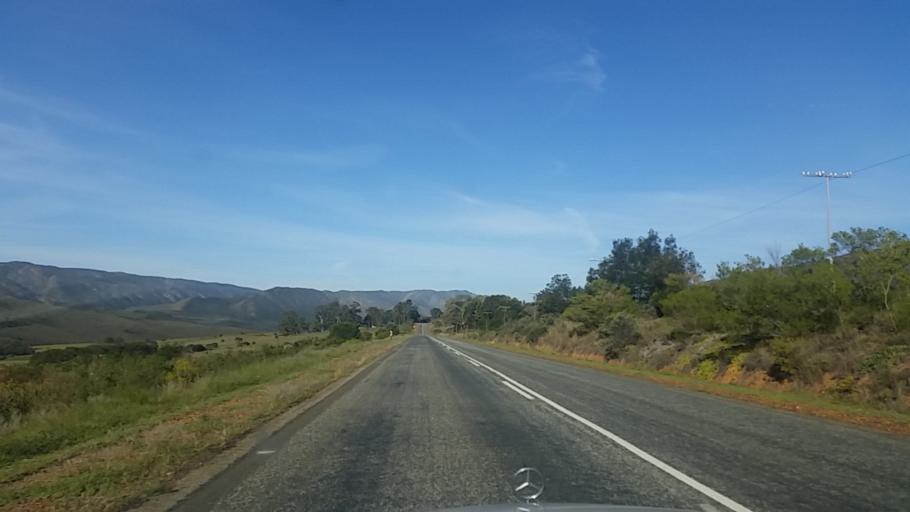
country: ZA
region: Western Cape
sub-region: Eden District Municipality
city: Knysna
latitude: -33.7746
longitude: 22.9099
